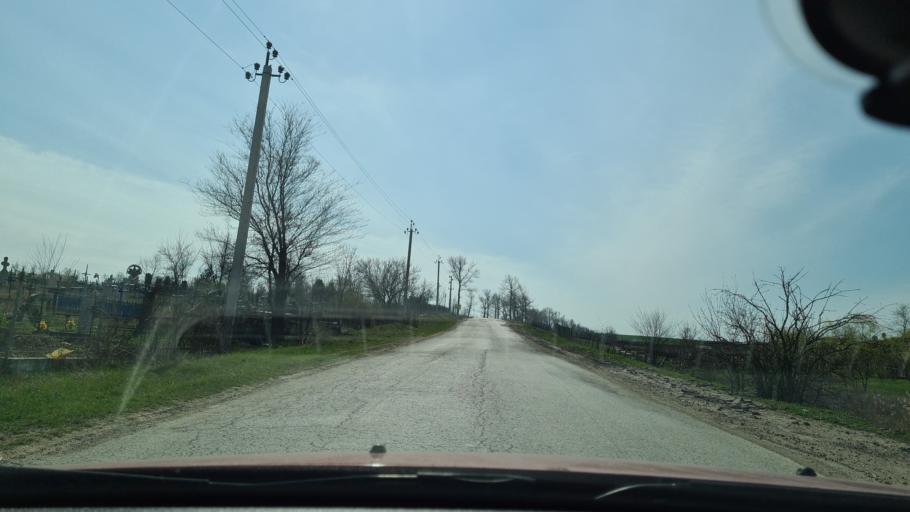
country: MD
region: Ungheni
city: Ungheni
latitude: 47.3167
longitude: 27.9016
